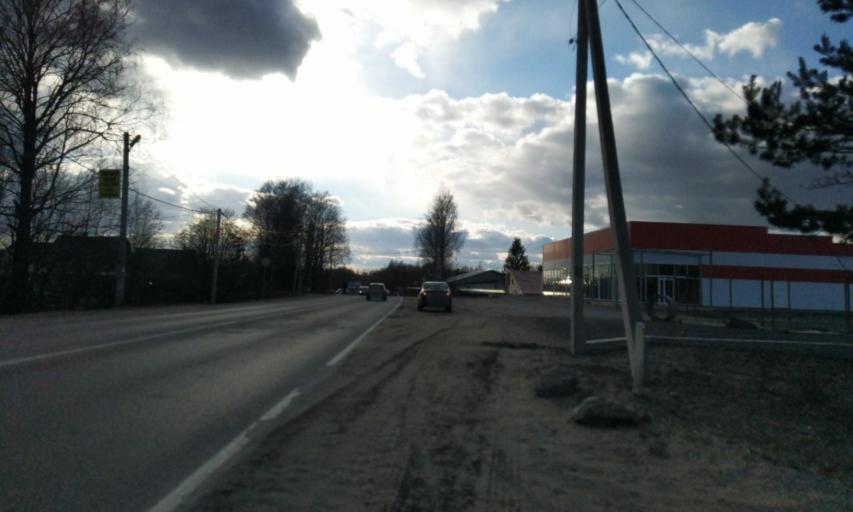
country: RU
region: Leningrad
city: Bugry
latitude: 60.1105
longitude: 30.4288
